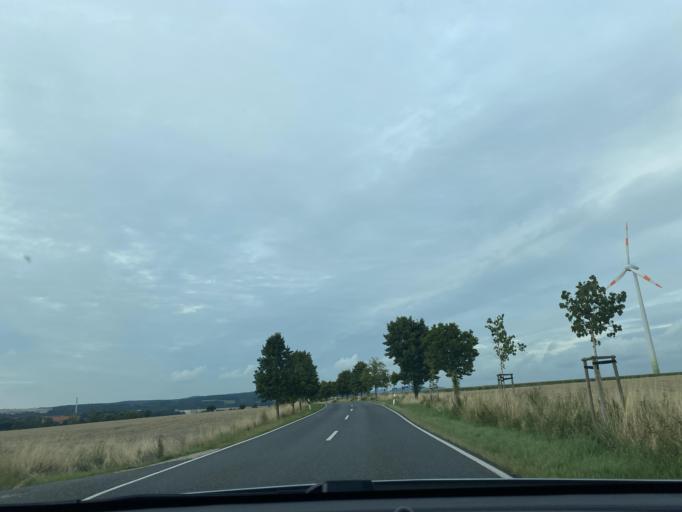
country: DE
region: Saxony
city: Bernstadt
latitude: 51.0347
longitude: 14.8139
